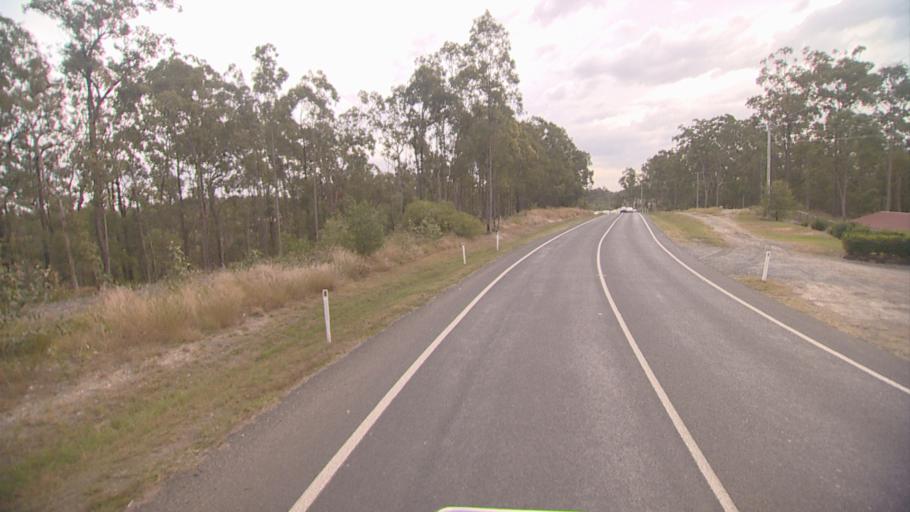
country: AU
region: Queensland
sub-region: Logan
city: Windaroo
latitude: -27.7263
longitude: 153.1670
